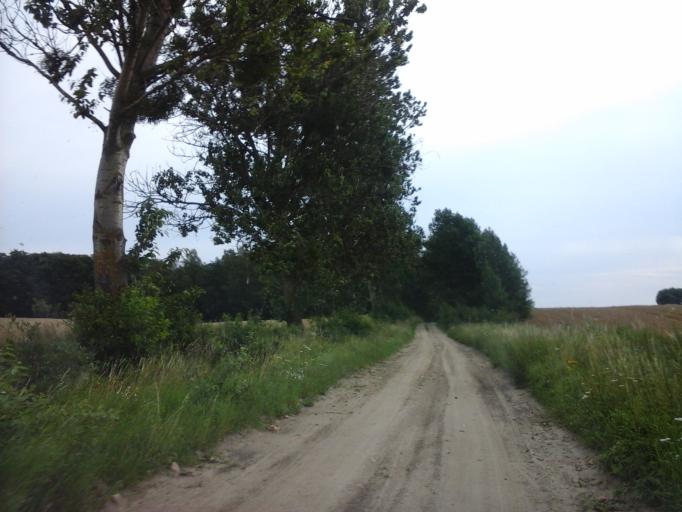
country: PL
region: West Pomeranian Voivodeship
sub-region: Powiat choszczenski
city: Recz
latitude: 53.2171
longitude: 15.5863
